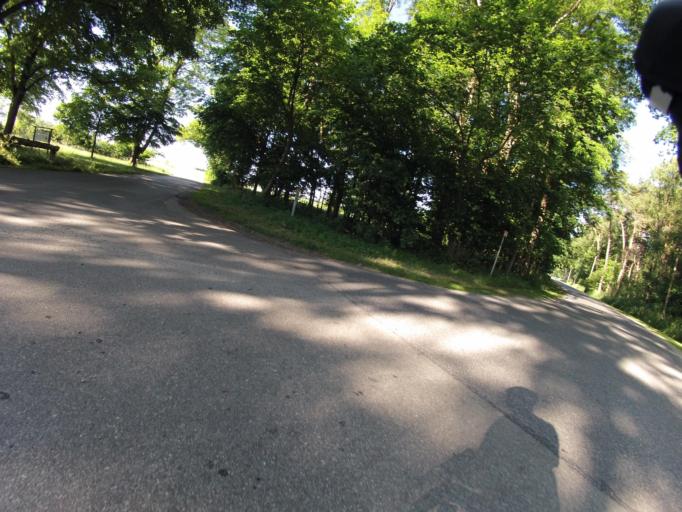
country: DE
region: Lower Saxony
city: Salzbergen
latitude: 52.3007
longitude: 7.3209
